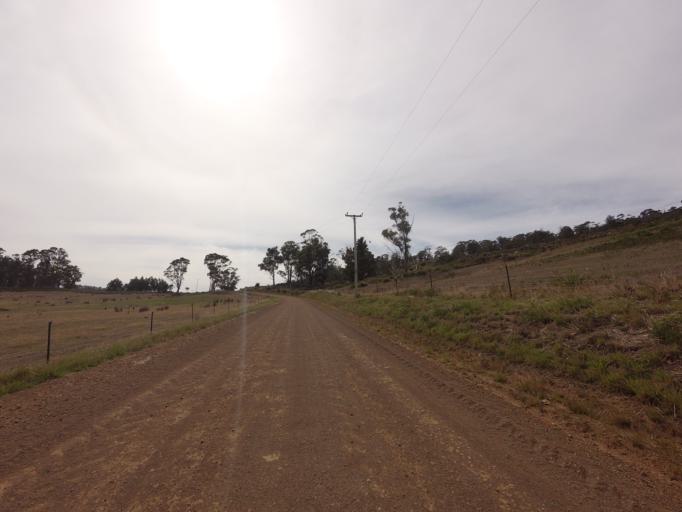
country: AU
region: Tasmania
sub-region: Sorell
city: Sorell
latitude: -42.4809
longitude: 147.5833
